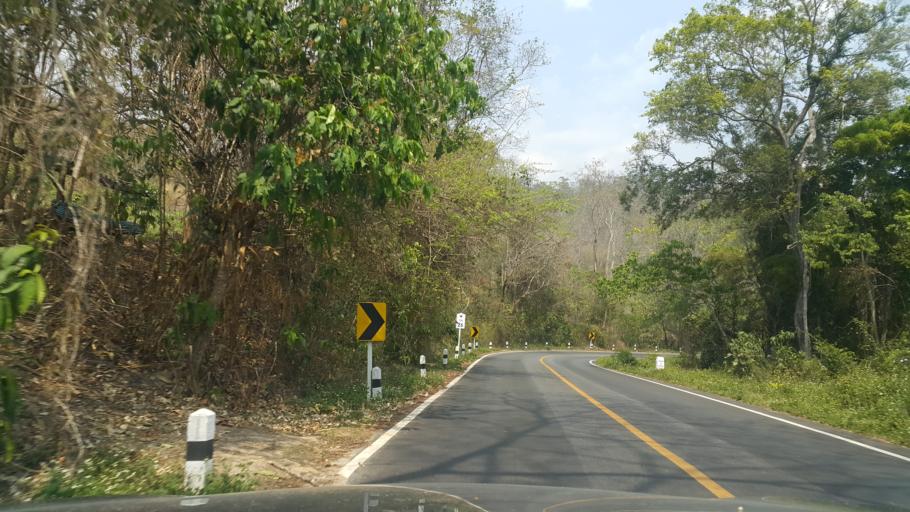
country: TH
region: Lamphun
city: Thung Hua Chang
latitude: 17.9065
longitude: 99.1158
